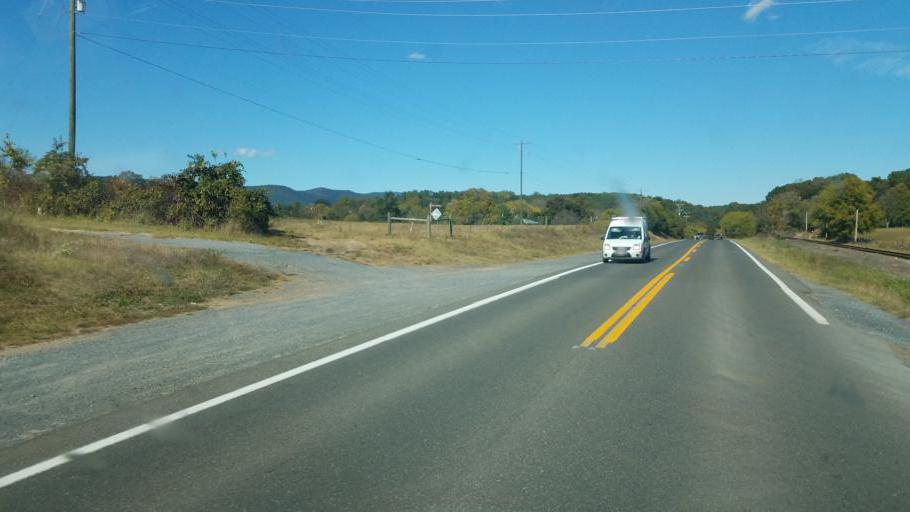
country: US
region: Virginia
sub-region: Shenandoah County
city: Woodstock
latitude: 38.8114
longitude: -78.3451
